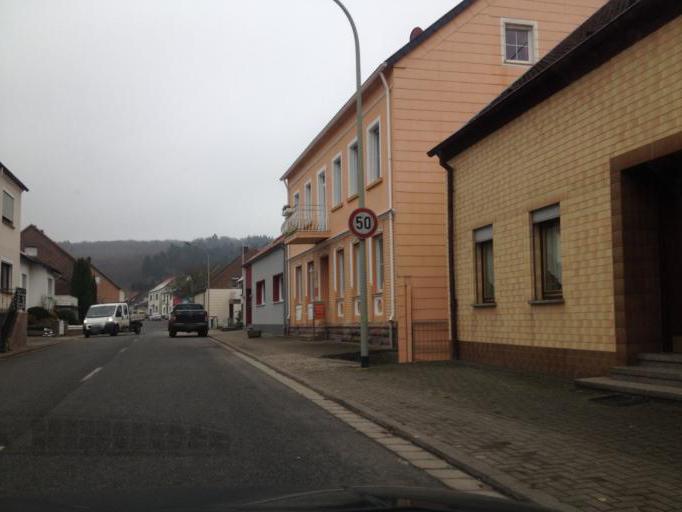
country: DE
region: Saarland
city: Hangard
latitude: 49.3940
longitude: 7.2468
